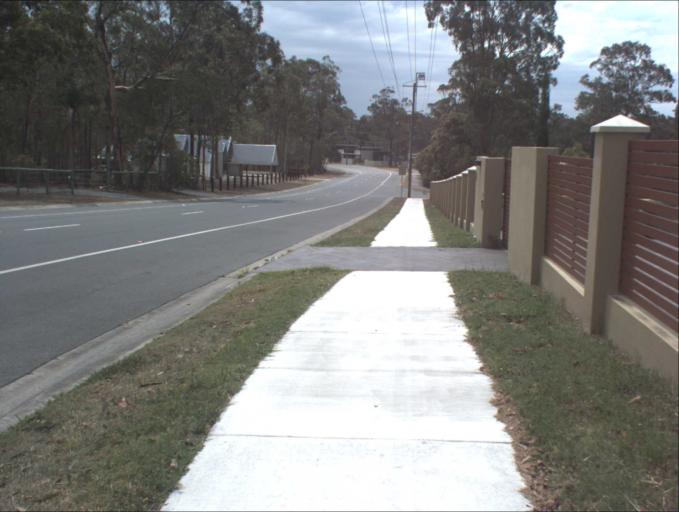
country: AU
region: Queensland
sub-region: Logan
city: Beenleigh
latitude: -27.6697
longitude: 153.2225
